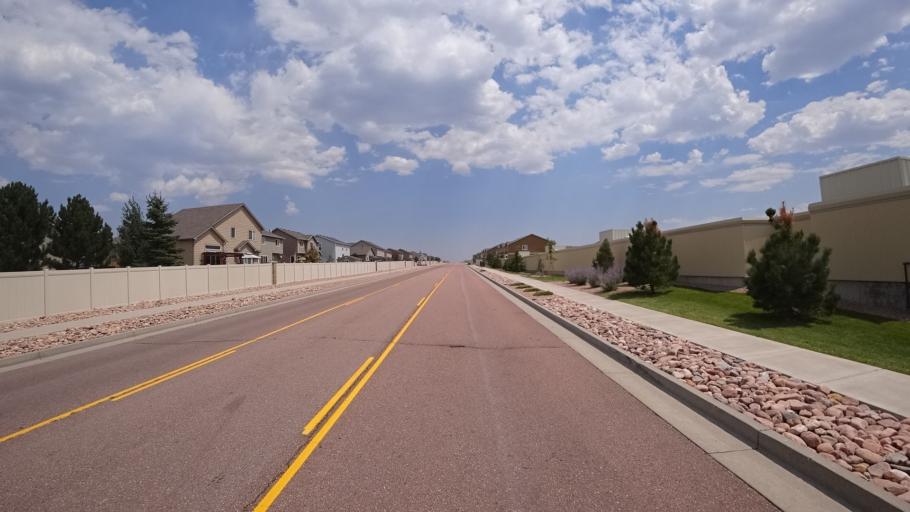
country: US
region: Colorado
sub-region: El Paso County
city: Black Forest
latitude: 38.9437
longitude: -104.6947
